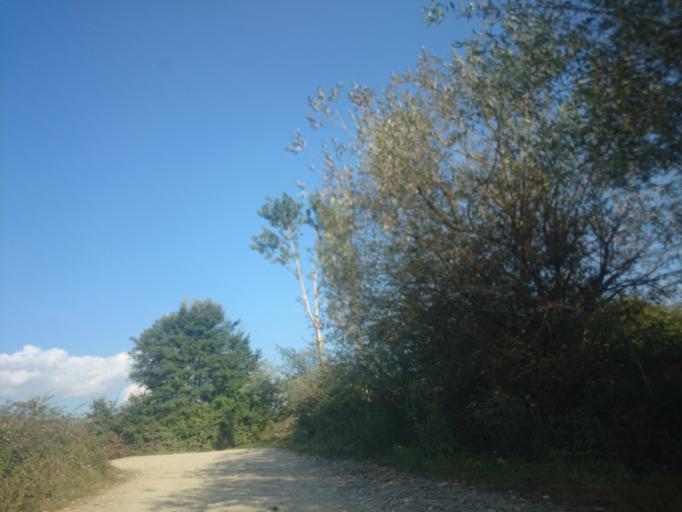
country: AL
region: Diber
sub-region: Rrethi i Dibres
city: Kastriot
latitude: 41.7225
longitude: 20.3682
